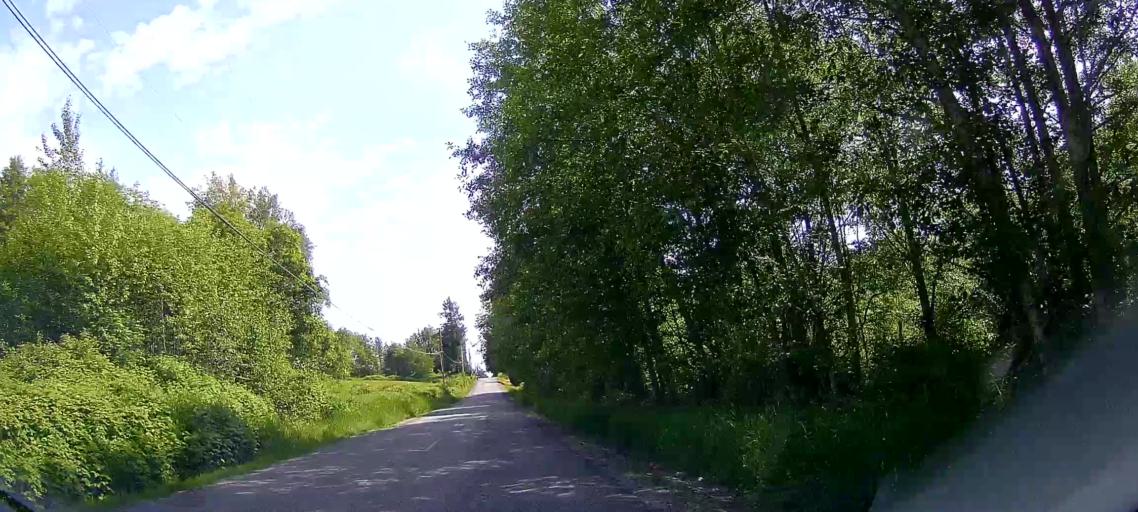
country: US
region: Washington
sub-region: Skagit County
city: Burlington
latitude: 48.5648
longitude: -122.3618
